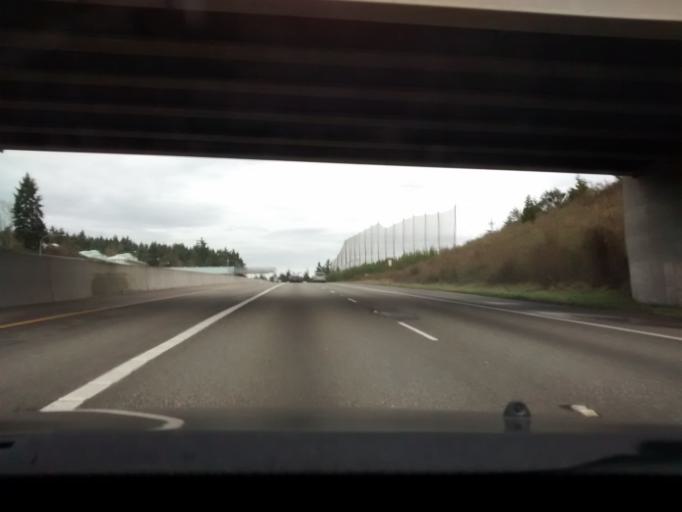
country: US
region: Washington
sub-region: Pierce County
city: Wollochet
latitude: 47.2797
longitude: -122.5606
